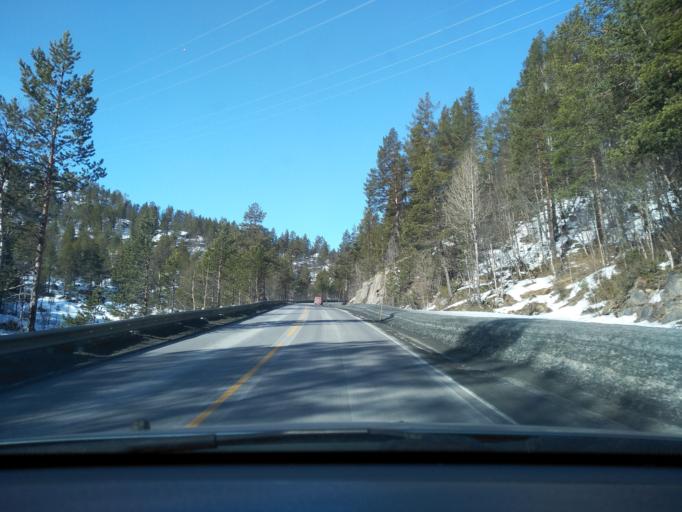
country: NO
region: Aust-Agder
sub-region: Bykle
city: Hovden
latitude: 59.7332
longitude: 7.4577
